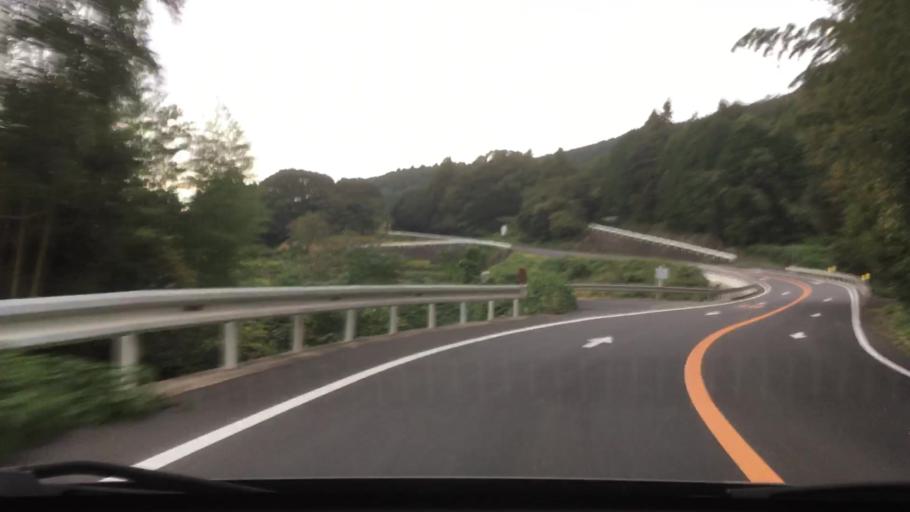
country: JP
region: Nagasaki
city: Sasebo
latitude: 33.0390
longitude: 129.6830
